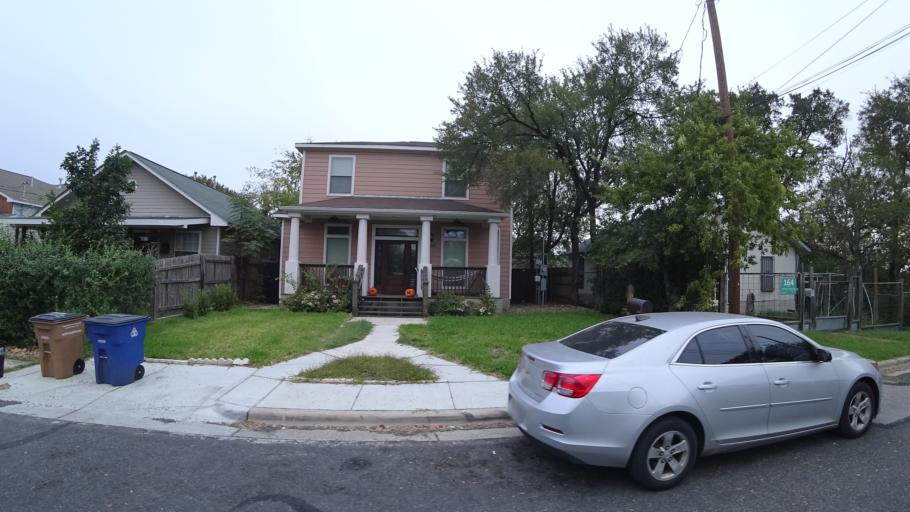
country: US
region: Texas
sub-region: Travis County
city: Austin
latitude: 30.2660
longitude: -97.7162
